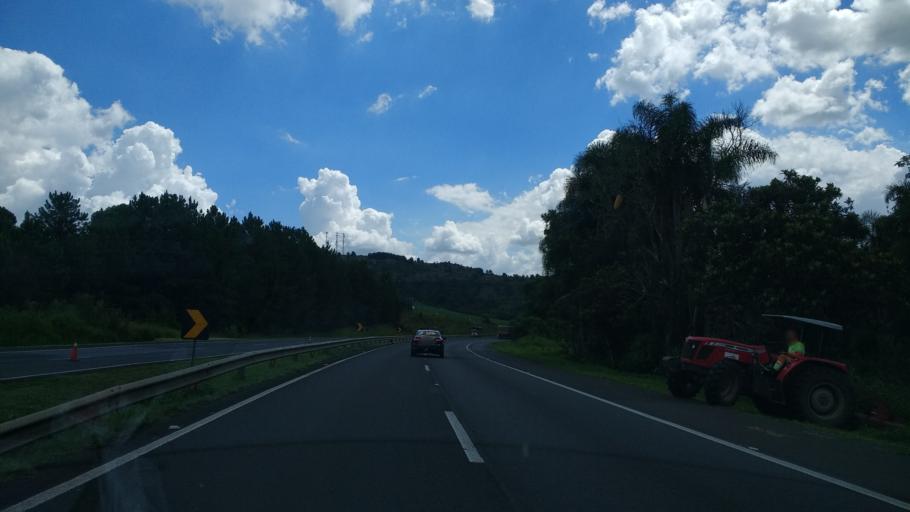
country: BR
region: Parana
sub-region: Palmeira
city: Palmeira
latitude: -25.2668
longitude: -49.9649
